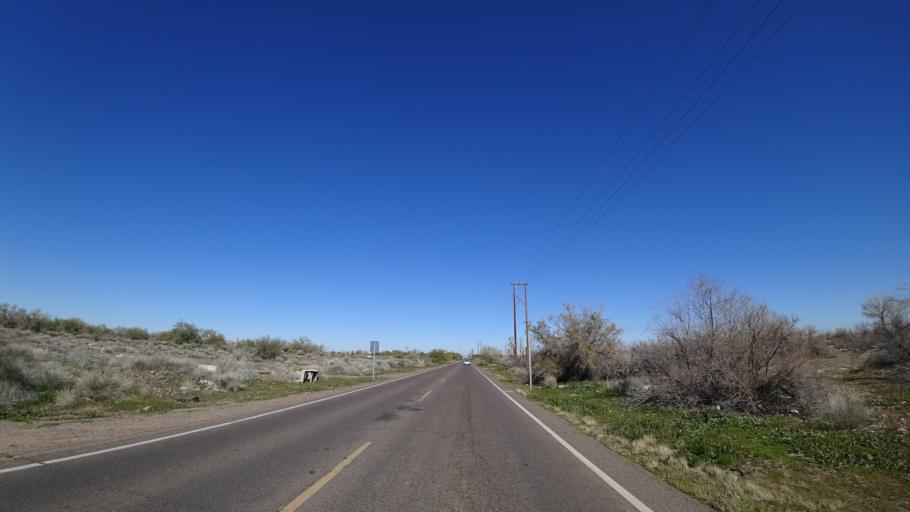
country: US
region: Arizona
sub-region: Maricopa County
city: Tolleson
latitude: 33.3849
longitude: -112.2543
